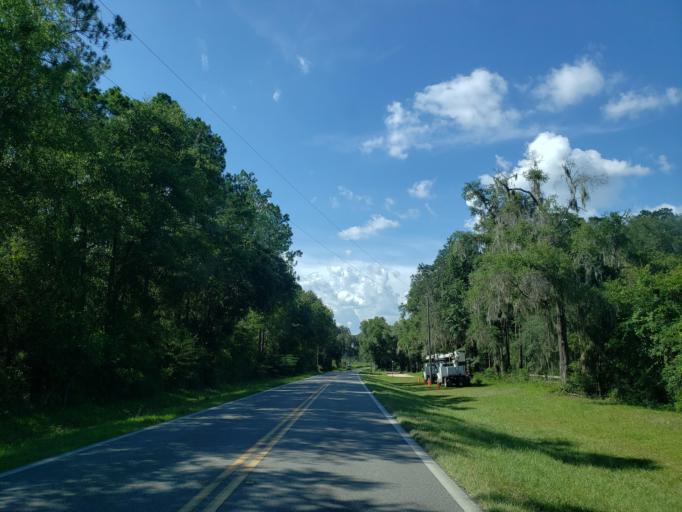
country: US
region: Georgia
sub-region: Lowndes County
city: Valdosta
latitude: 30.6235
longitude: -83.2565
